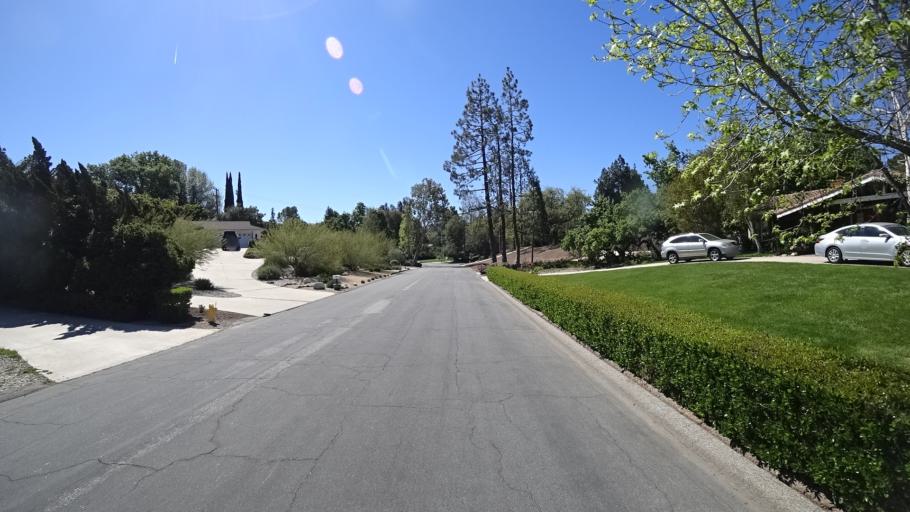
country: US
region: California
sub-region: Ventura County
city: Thousand Oaks
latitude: 34.1918
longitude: -118.8504
